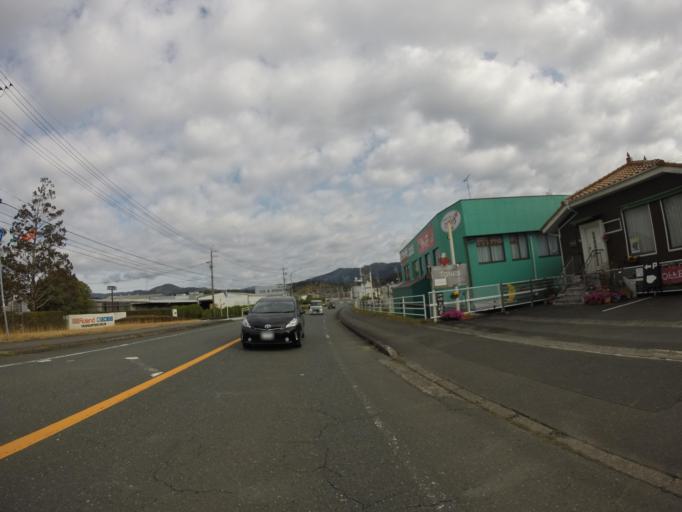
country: JP
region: Shizuoka
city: Hamakita
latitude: 34.8107
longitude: 137.6853
